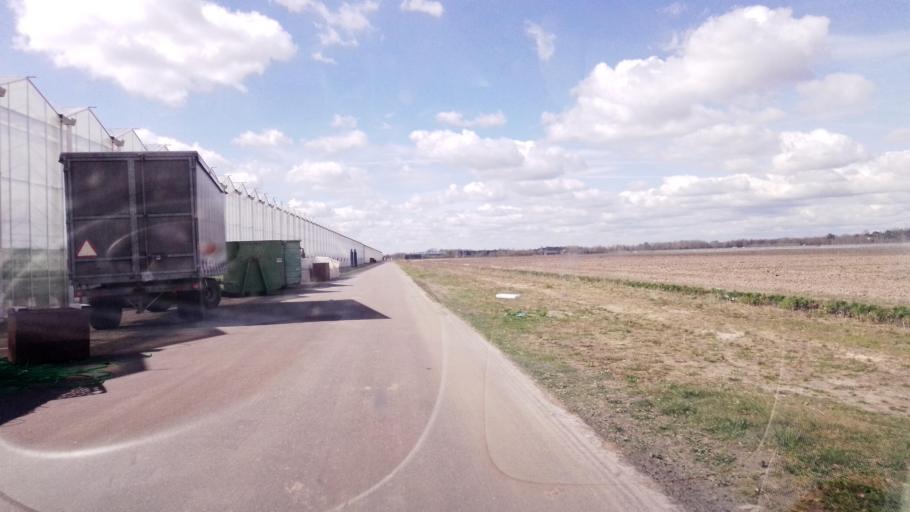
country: NL
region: Limburg
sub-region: Gemeente Peel en Maas
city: Maasbree
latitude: 51.3861
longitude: 6.0690
